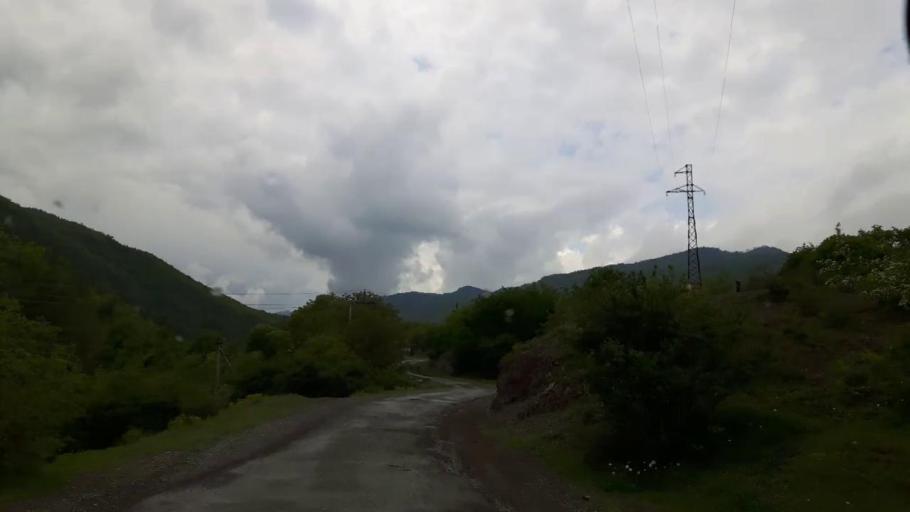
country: GE
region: Shida Kartli
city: Gori
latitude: 41.8923
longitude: 44.0168
